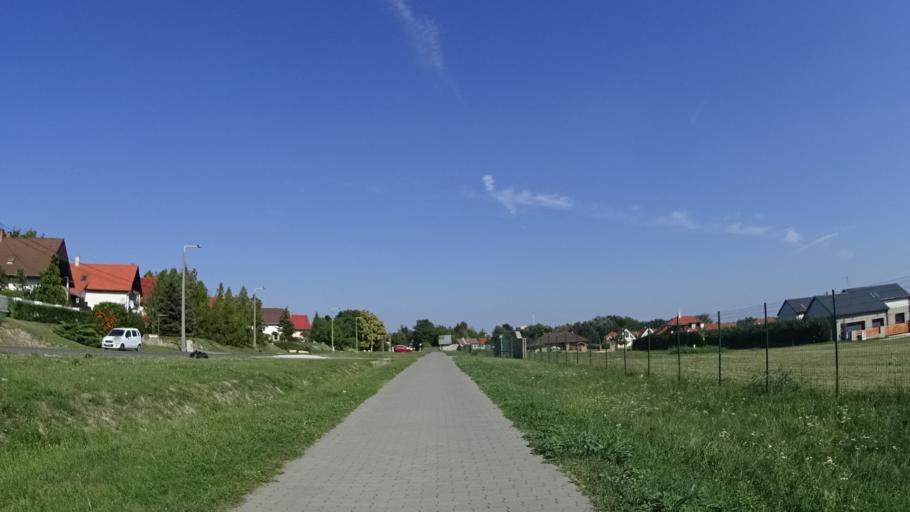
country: HU
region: Fejer
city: Velence
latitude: 47.2378
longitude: 18.6472
